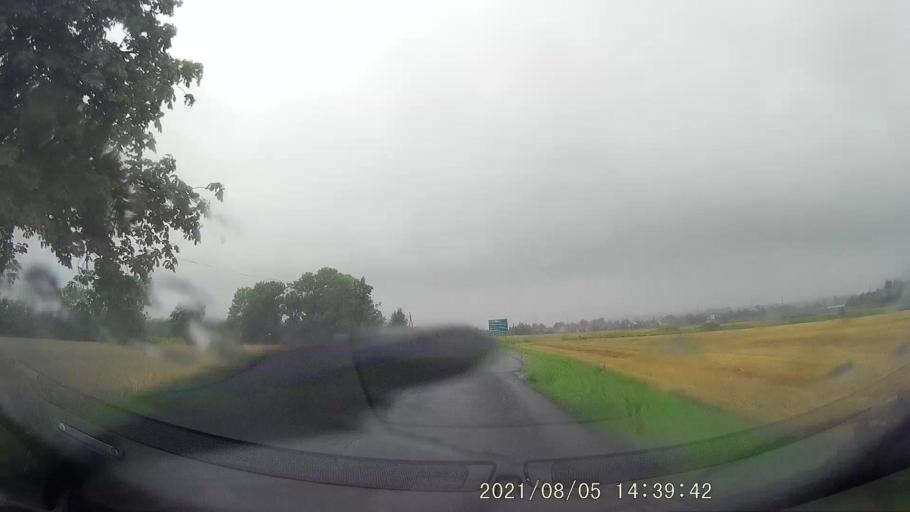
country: PL
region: Opole Voivodeship
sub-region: Powiat nyski
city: Sidzina
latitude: 50.4726
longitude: 17.4402
